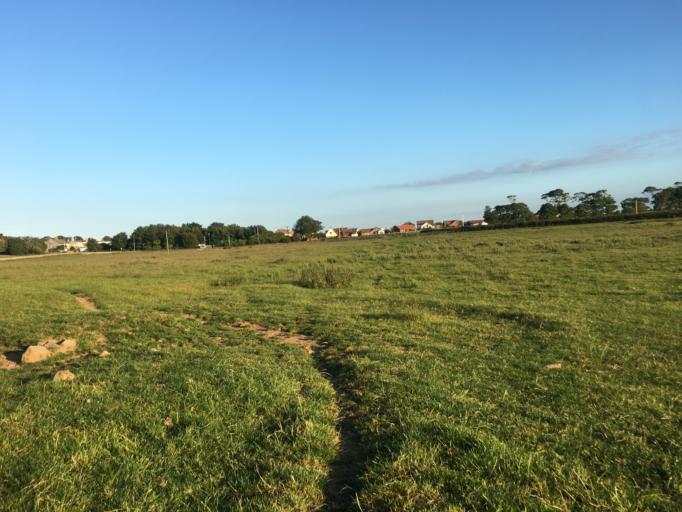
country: GB
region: England
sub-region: Northumberland
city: North Sunderland
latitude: 55.5802
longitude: -1.6713
